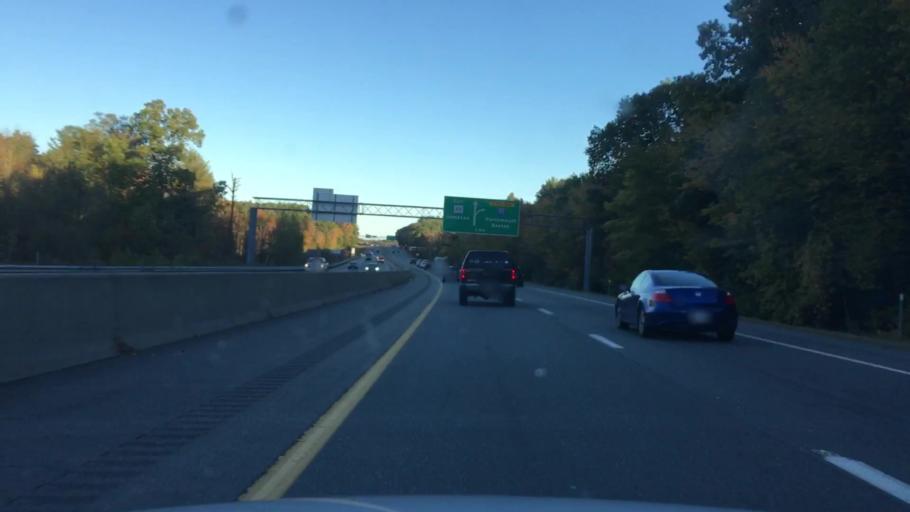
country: US
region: New Hampshire
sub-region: Rockingham County
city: Hampton
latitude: 42.9656
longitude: -70.8821
